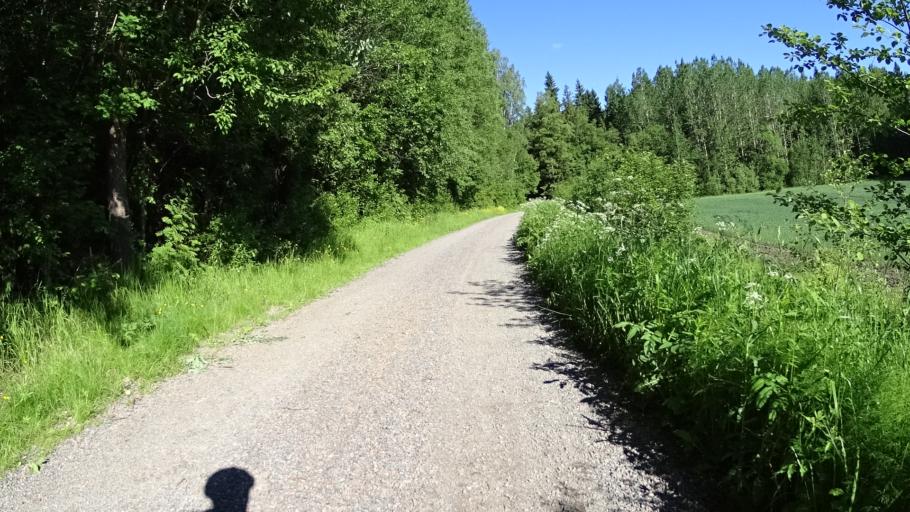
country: FI
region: Uusimaa
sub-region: Helsinki
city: Kilo
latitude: 60.2946
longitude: 24.8119
